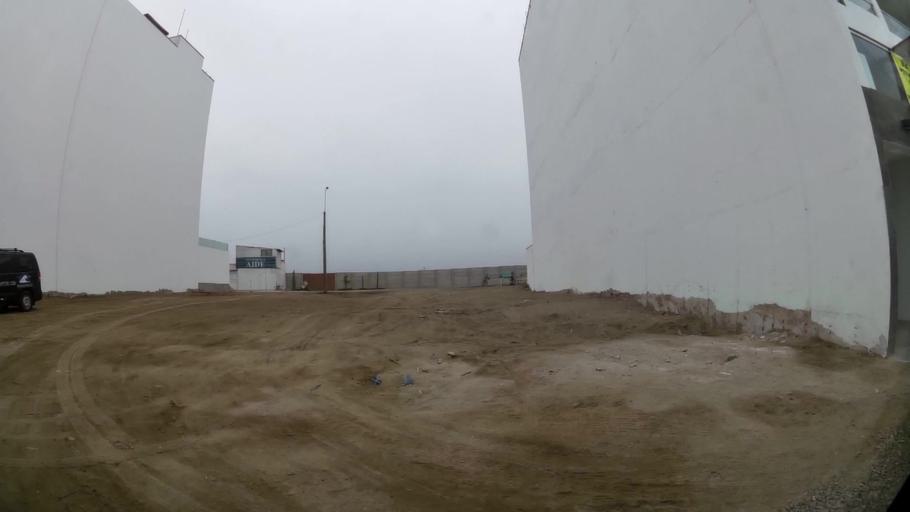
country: PE
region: Lima
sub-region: Lima
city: Punta Hermosa
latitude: -12.3249
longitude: -76.8343
